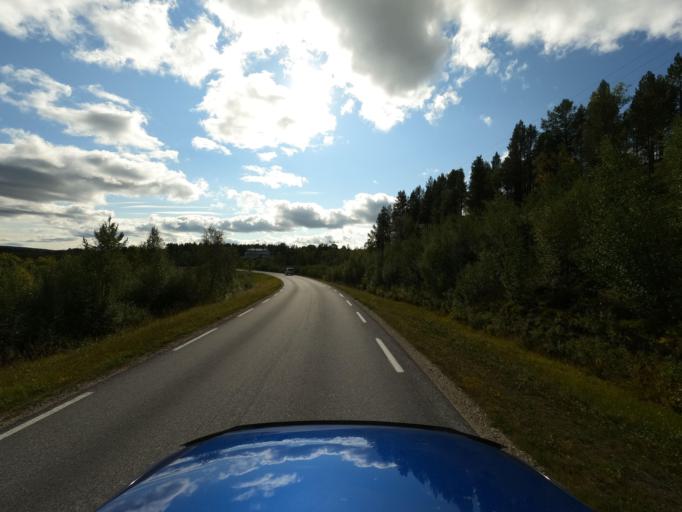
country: NO
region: Finnmark Fylke
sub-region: Karasjok
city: Karasjohka
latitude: 69.4032
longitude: 25.8113
